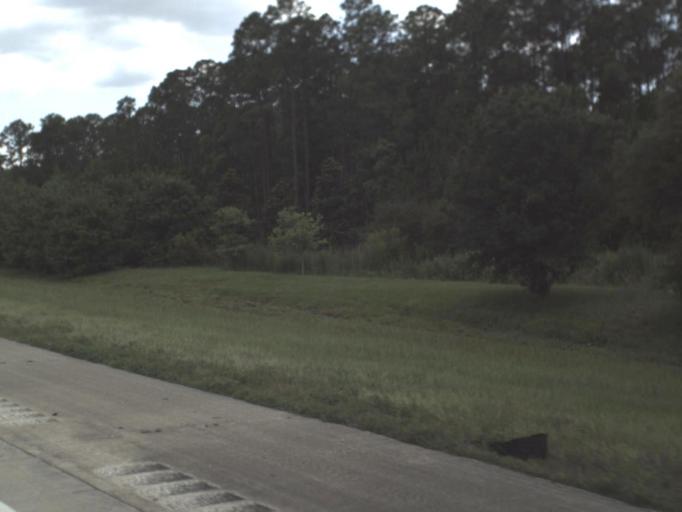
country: US
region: Florida
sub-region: Saint Johns County
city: Palm Valley
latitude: 30.1790
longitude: -81.5151
